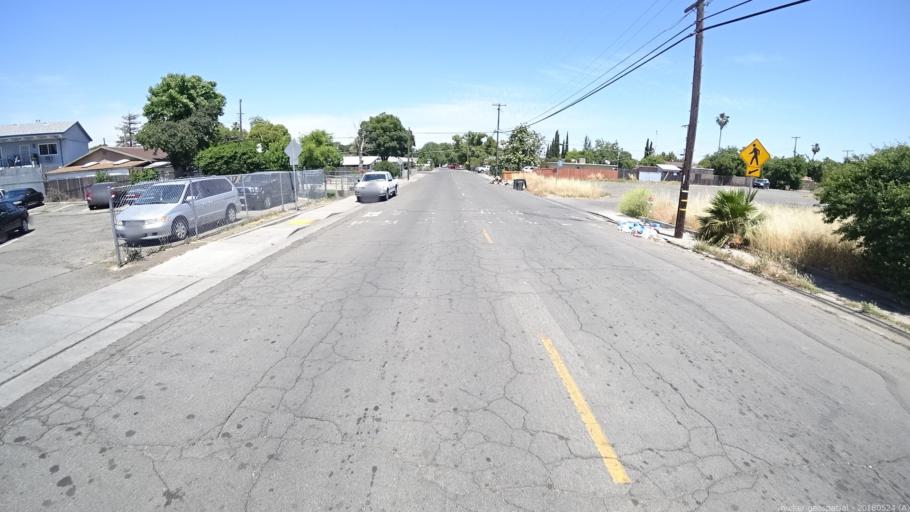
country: US
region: California
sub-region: Sacramento County
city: Sacramento
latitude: 38.6196
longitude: -121.4594
